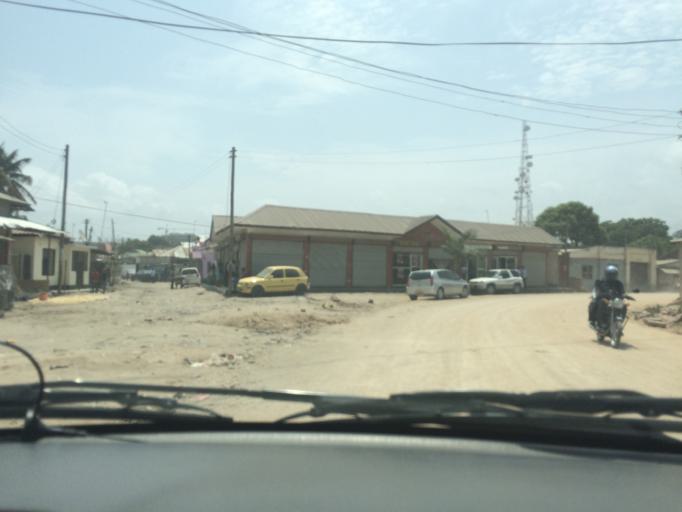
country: TZ
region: Dar es Salaam
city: Magomeni
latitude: -6.7698
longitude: 39.2662
